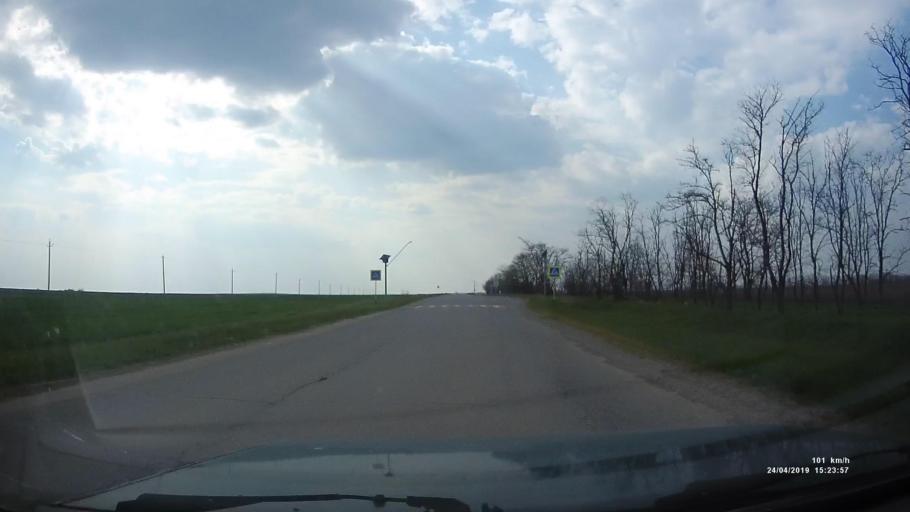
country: RU
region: Rostov
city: Remontnoye
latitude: 46.5456
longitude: 43.0791
